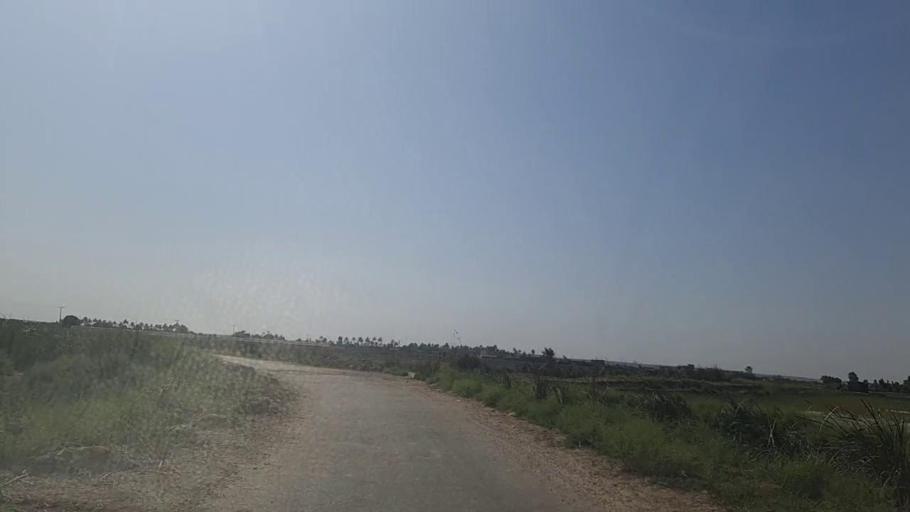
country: PK
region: Sindh
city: Thatta
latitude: 24.6366
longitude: 67.9018
